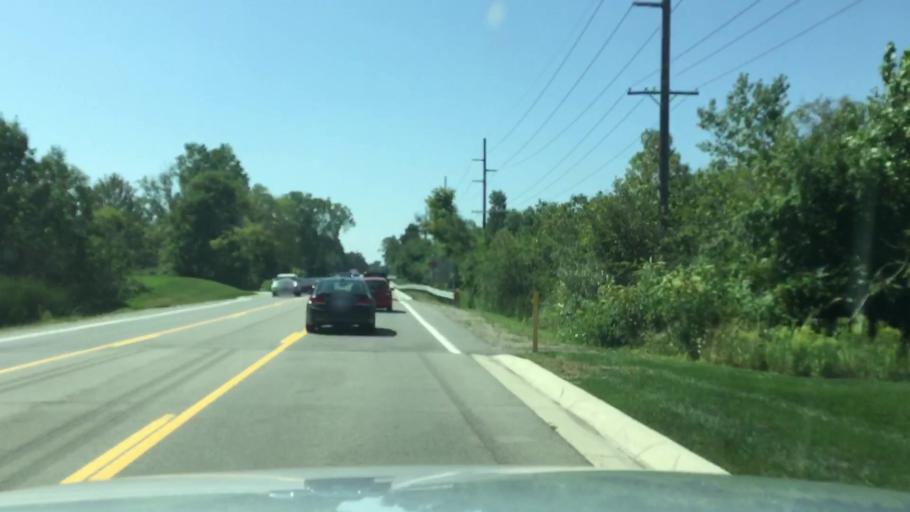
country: US
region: Michigan
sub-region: Oakland County
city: West Bloomfield Township
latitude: 42.5412
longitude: -83.4238
